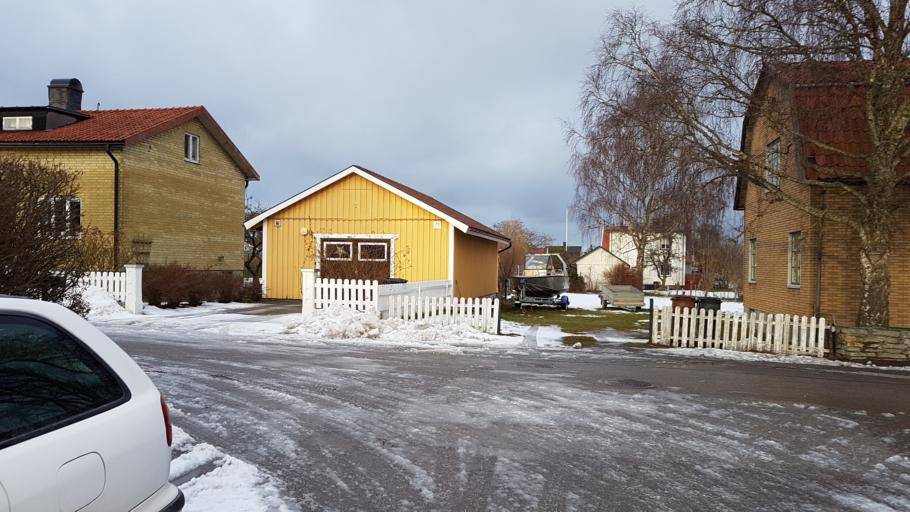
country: SE
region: Gotland
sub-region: Gotland
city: Visby
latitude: 57.6213
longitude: 18.2895
